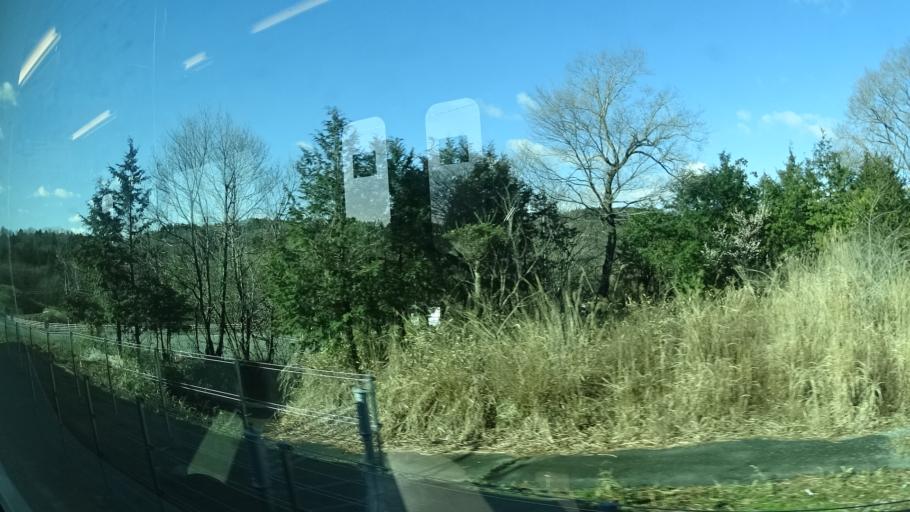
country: JP
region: Fukushima
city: Namie
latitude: 37.3736
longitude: 140.9910
